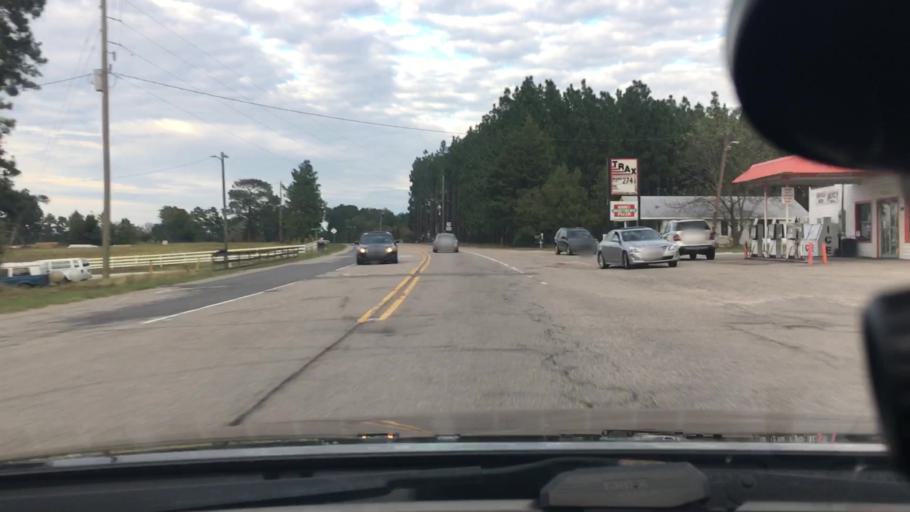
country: US
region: North Carolina
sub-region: Moore County
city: Carthage
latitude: 35.3620
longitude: -79.3207
